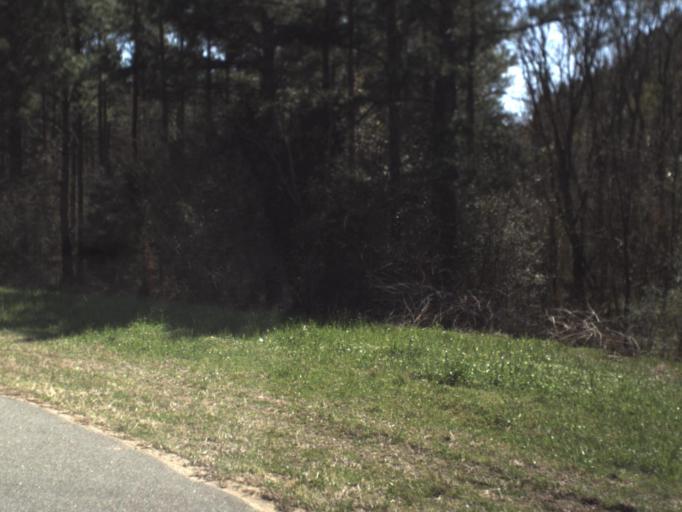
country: US
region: Florida
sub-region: Jackson County
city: Marianna
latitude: 30.8389
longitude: -85.3439
